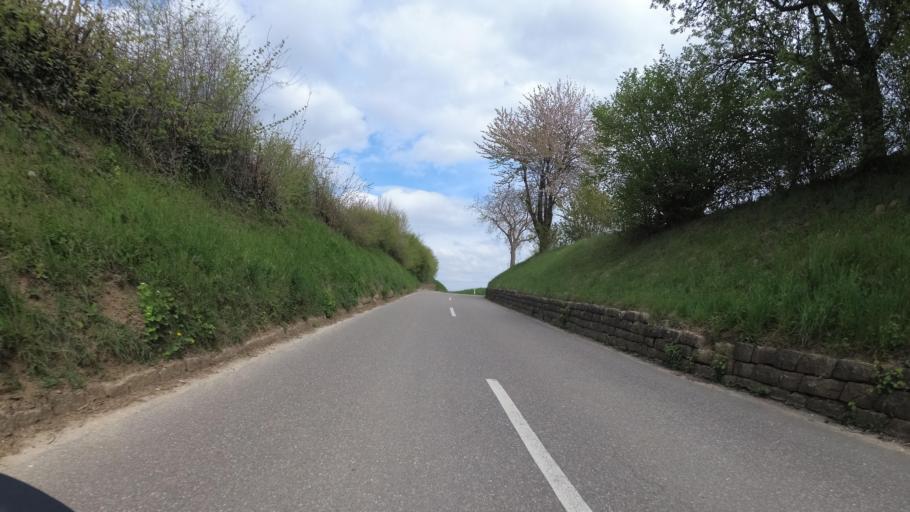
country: DE
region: Baden-Wuerttemberg
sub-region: Regierungsbezirk Stuttgart
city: Neuenstadt am Kocher
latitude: 49.2471
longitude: 9.3646
